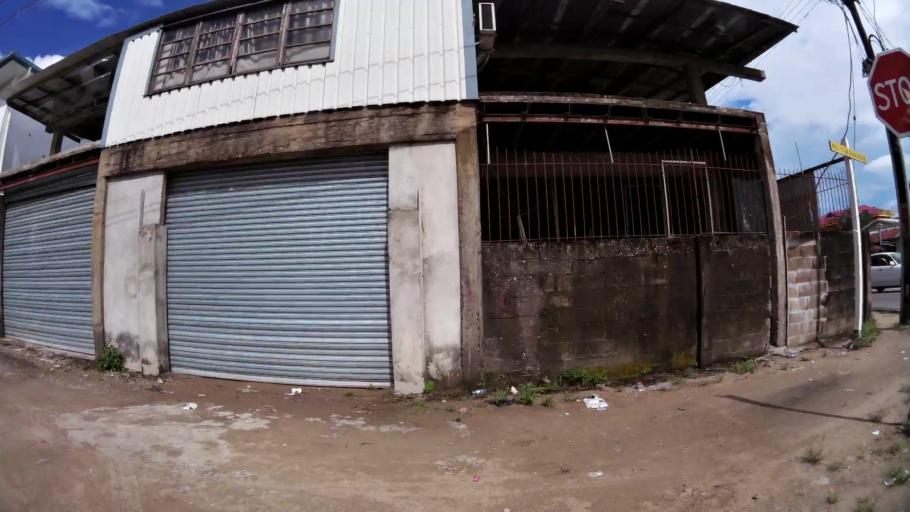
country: SR
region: Paramaribo
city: Paramaribo
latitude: 5.8354
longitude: -55.1478
